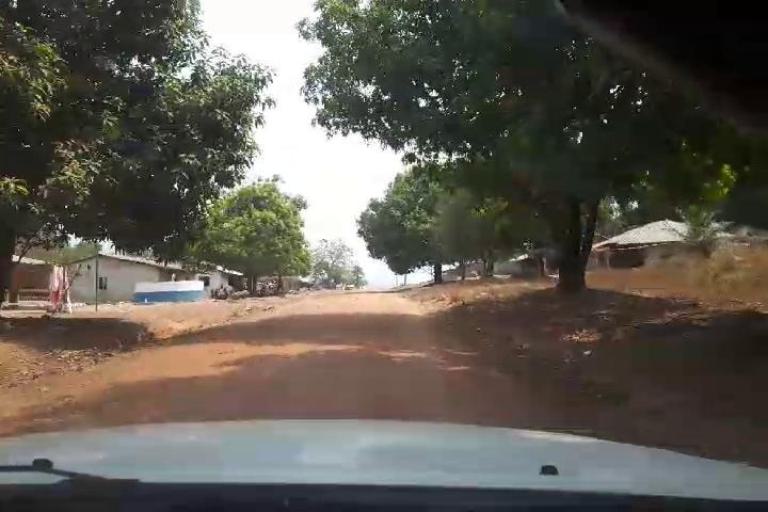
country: SL
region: Northern Province
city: Bumbuna
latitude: 9.0146
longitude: -11.7673
